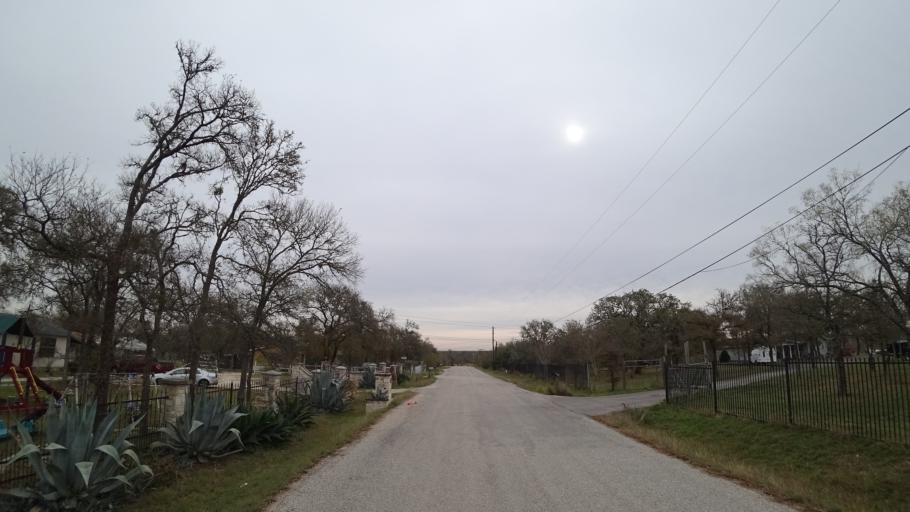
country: US
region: Texas
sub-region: Travis County
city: Garfield
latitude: 30.0976
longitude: -97.5733
